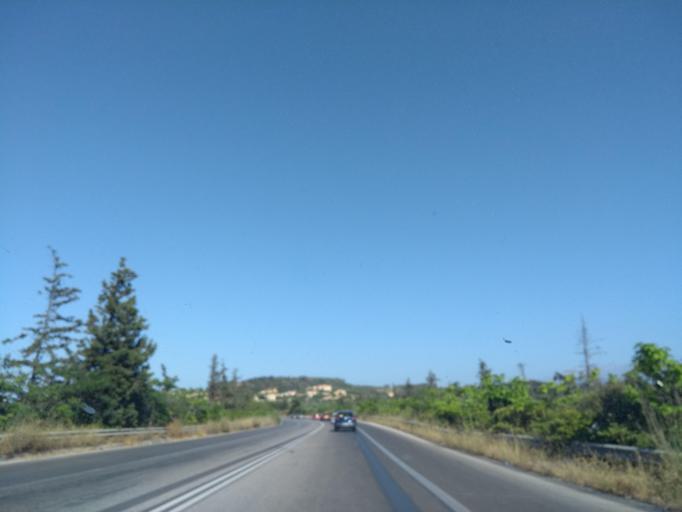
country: GR
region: Crete
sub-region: Nomos Chanias
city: Gerani
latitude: 35.5139
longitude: 23.8519
